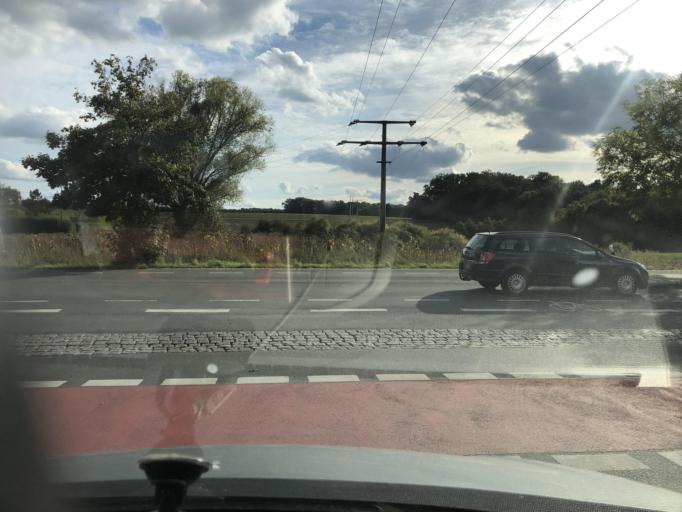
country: DE
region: Bavaria
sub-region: Regierungsbezirk Mittelfranken
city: Langenzenn
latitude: 49.4947
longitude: 10.8147
